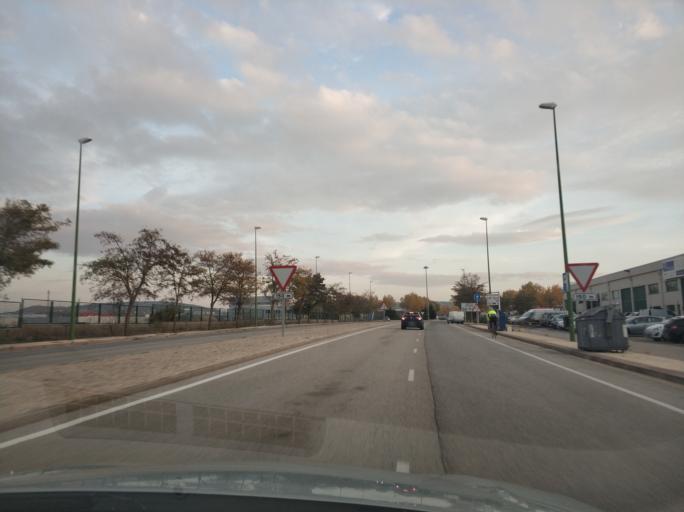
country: ES
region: Castille and Leon
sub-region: Provincia de Burgos
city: Sotragero
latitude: 42.3723
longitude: -3.7196
